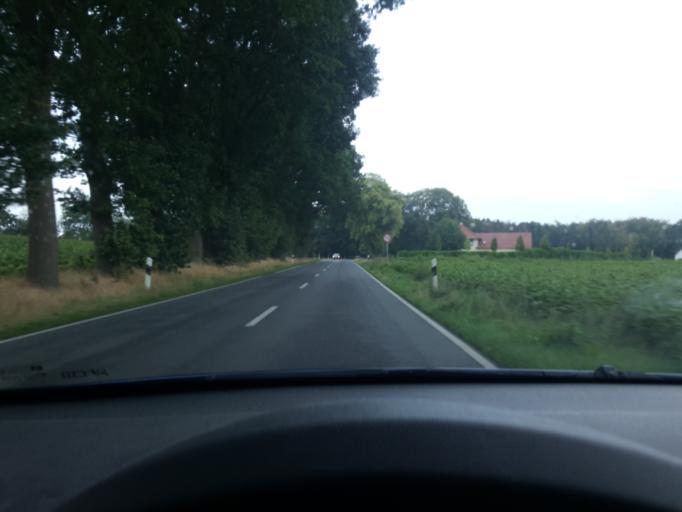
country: DE
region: Lower Saxony
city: Emstek
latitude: 52.8751
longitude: 8.1276
